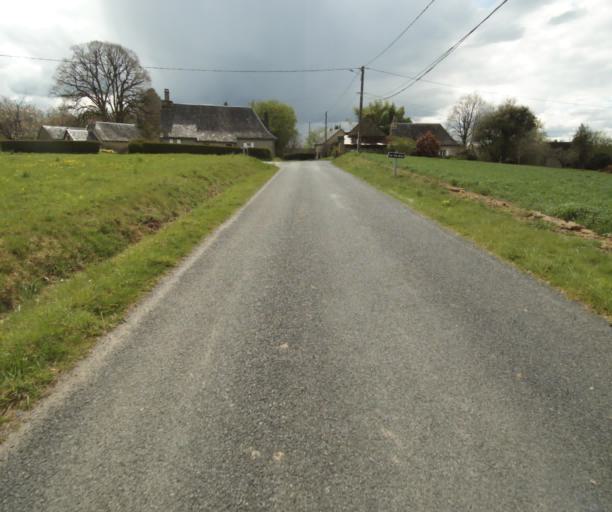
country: FR
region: Limousin
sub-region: Departement de la Correze
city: Laguenne
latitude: 45.2546
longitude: 1.8744
